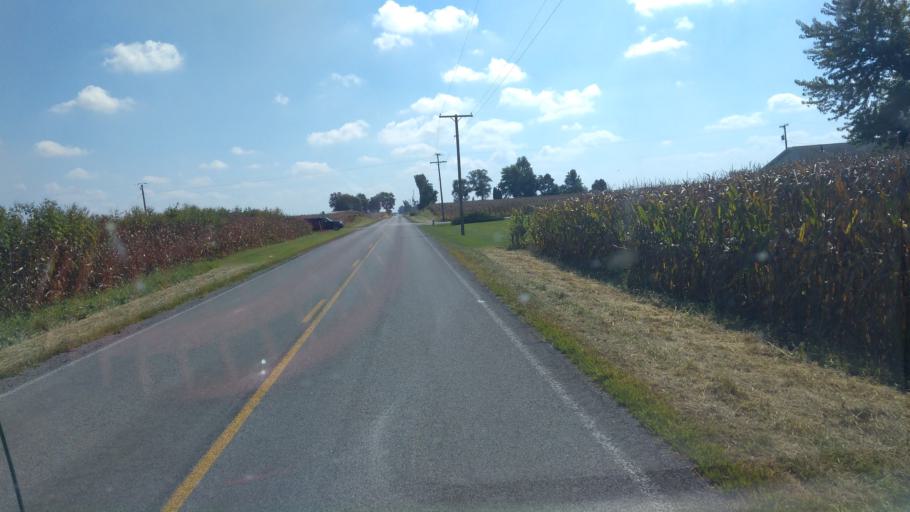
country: US
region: Ohio
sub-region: Hardin County
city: Ada
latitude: 40.7702
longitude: -83.7849
